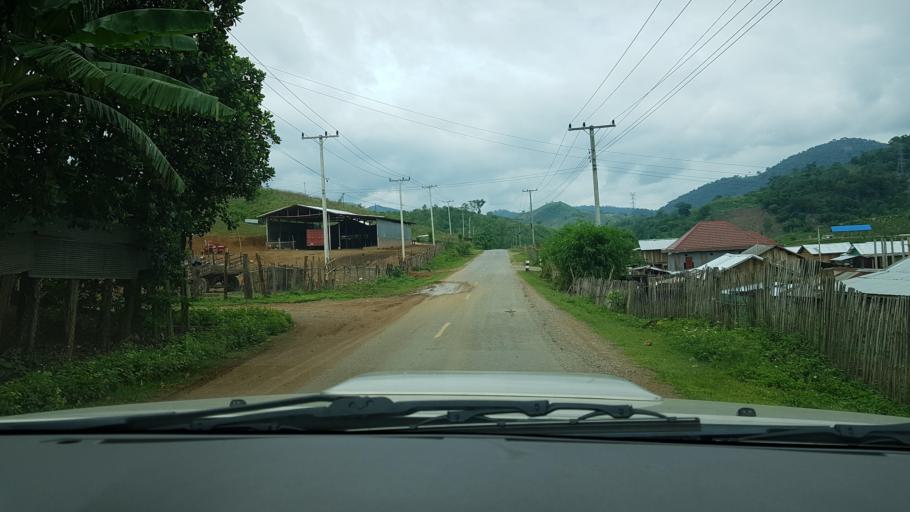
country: TH
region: Nan
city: Chaloem Phra Kiat
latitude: 19.9757
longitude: 101.2700
